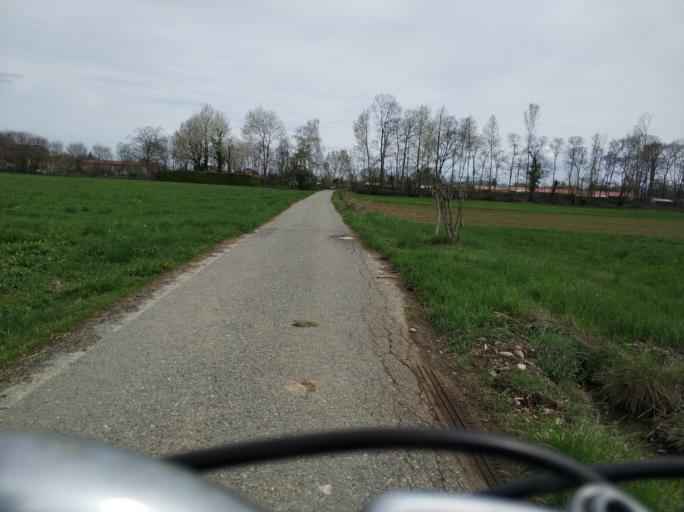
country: IT
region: Piedmont
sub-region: Provincia di Torino
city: Nole
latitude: 45.2320
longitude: 7.5711
